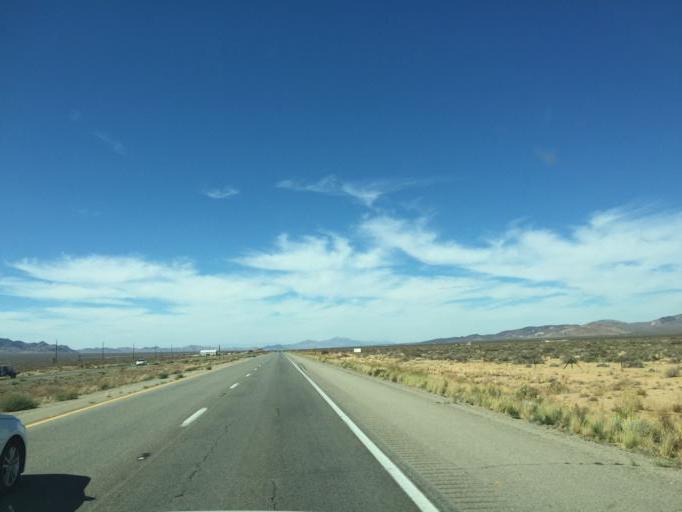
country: US
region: Arizona
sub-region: Mohave County
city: Dolan Springs
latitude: 35.5468
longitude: -114.3641
